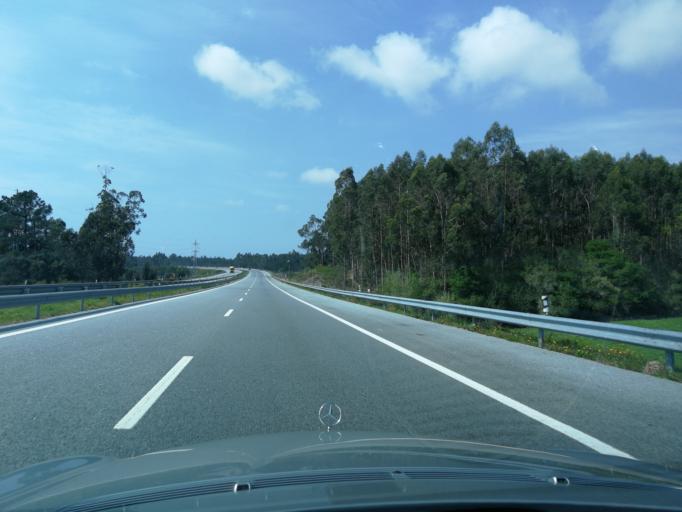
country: PT
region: Braga
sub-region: Vila Nova de Famalicao
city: Ribeirao
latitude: 41.3877
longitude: -8.5847
